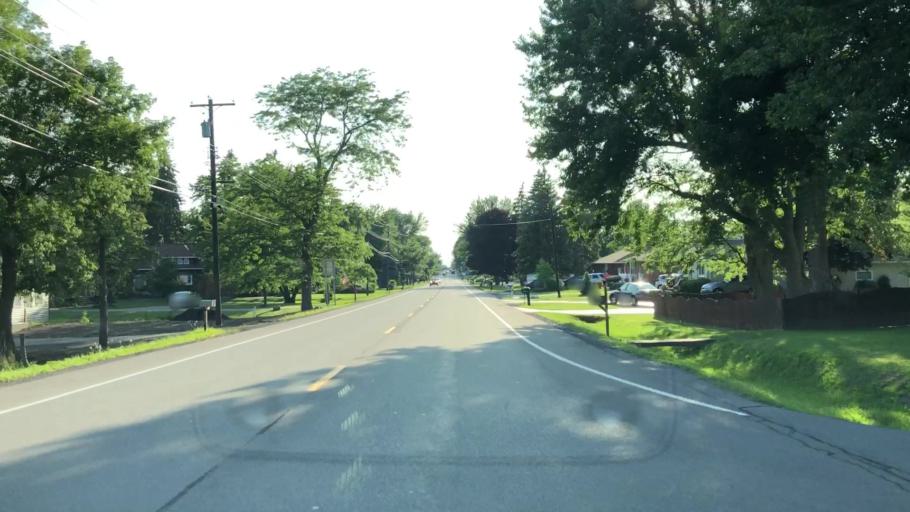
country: US
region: New York
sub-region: Erie County
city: Cheektowaga
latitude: 42.8576
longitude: -78.7241
